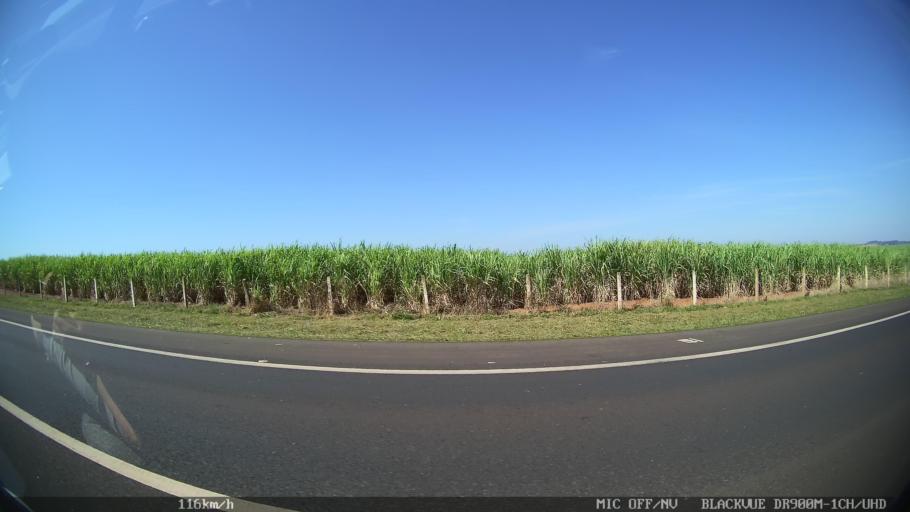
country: BR
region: Sao Paulo
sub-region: Batatais
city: Batatais
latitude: -20.8200
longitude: -47.5883
